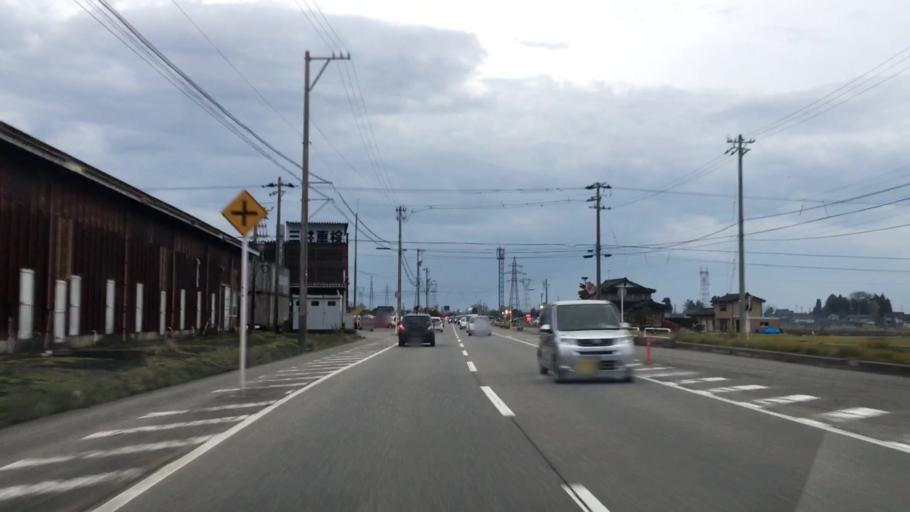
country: JP
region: Toyama
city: Kamiichi
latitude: 36.6863
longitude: 137.3108
